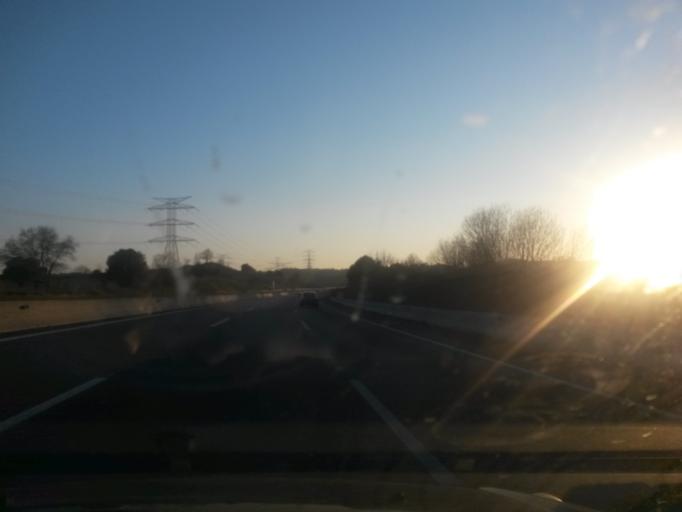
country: ES
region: Catalonia
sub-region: Provincia de Girona
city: Viladasens
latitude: 42.1071
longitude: 2.9107
